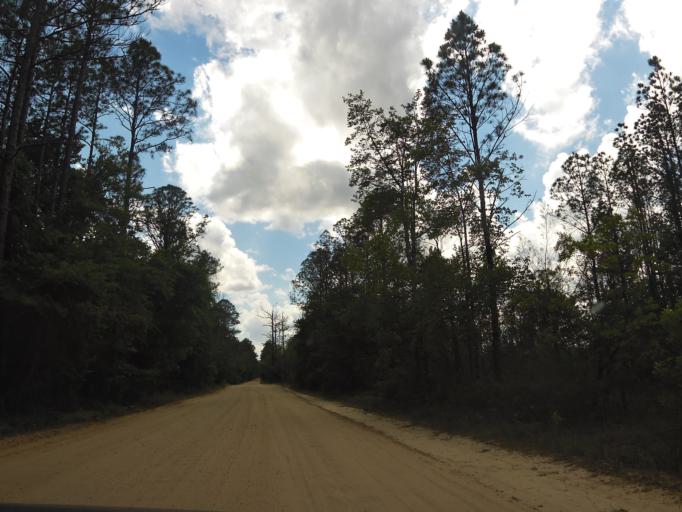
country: US
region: Florida
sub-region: Clay County
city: Asbury Lake
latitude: 29.8952
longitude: -81.8648
